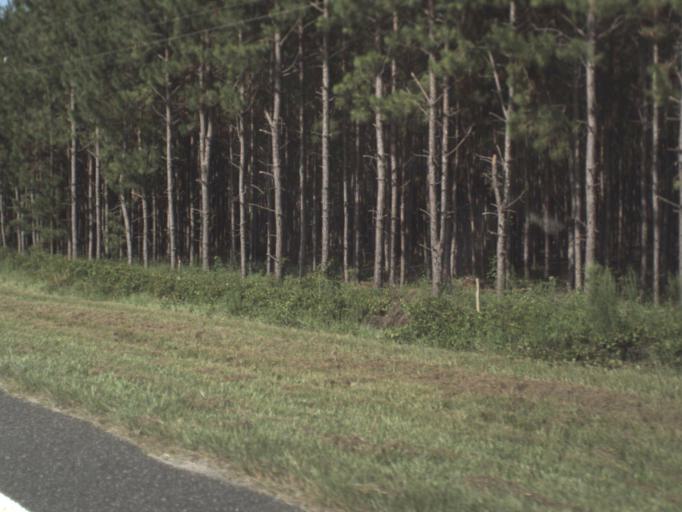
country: US
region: Florida
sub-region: Columbia County
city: Lake City
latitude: 30.0198
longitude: -82.7103
